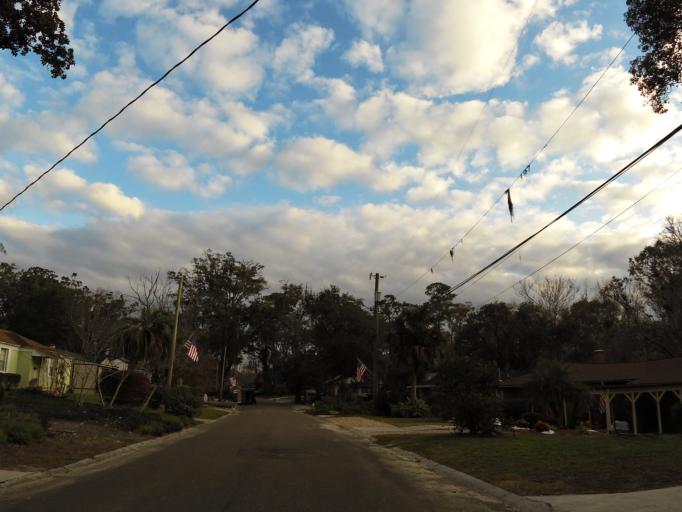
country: US
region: Florida
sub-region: Duval County
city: Jacksonville
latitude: 30.2925
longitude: -81.7188
